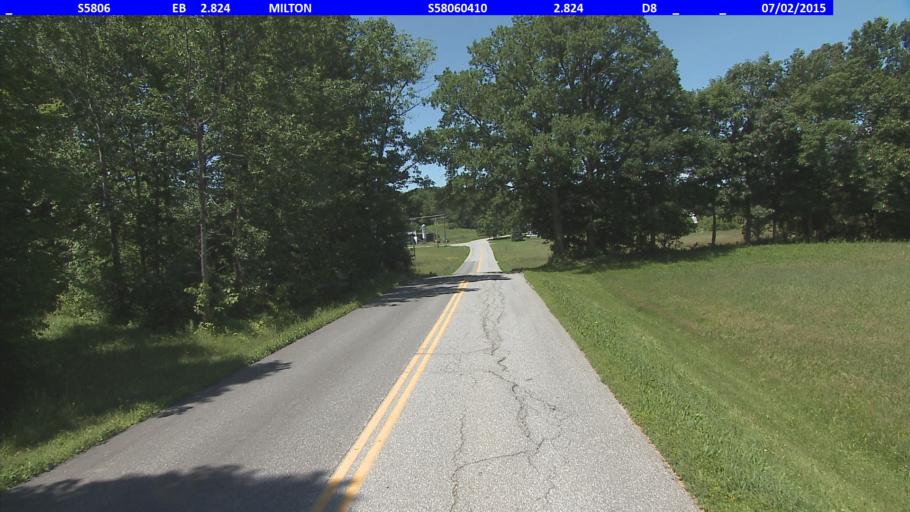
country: US
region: Vermont
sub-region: Chittenden County
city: Milton
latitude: 44.6677
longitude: -73.1638
